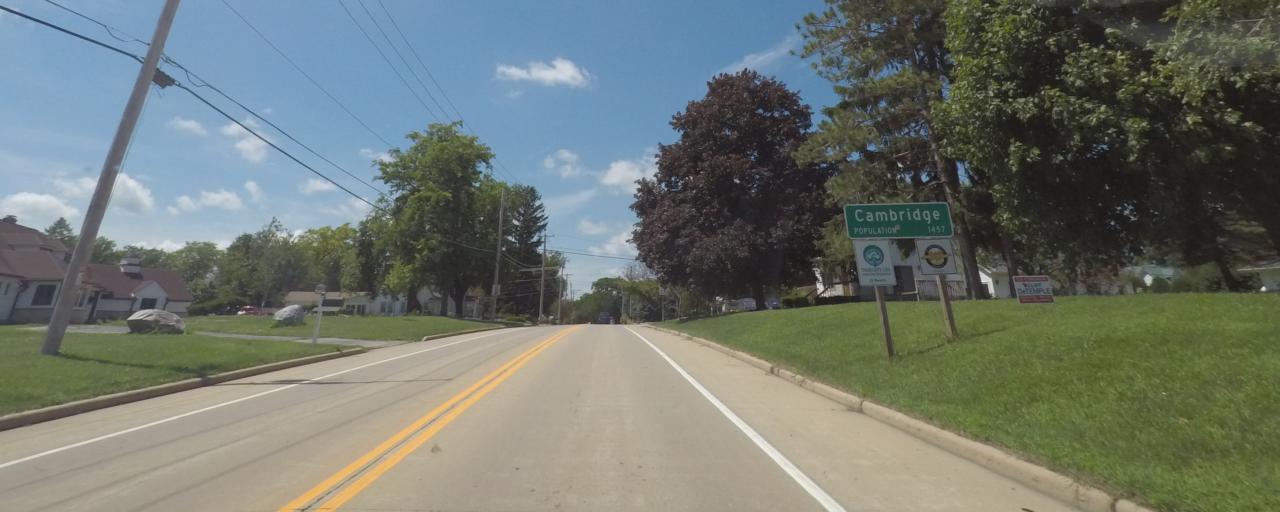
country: US
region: Wisconsin
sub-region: Jefferson County
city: Cambridge
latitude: 43.0020
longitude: -89.0105
